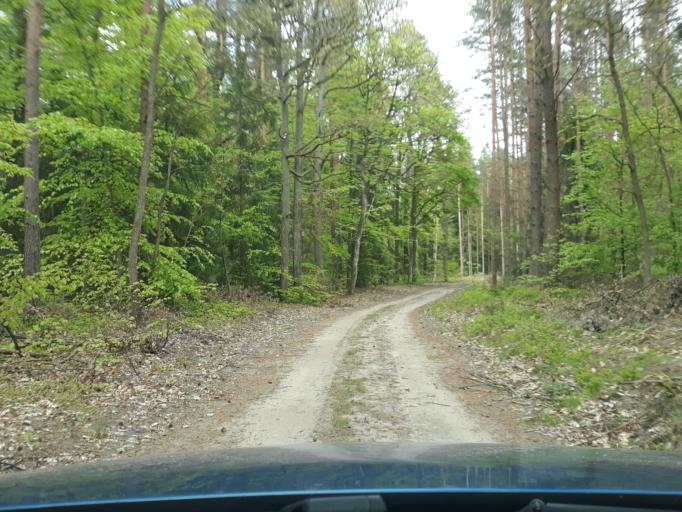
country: PL
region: Pomeranian Voivodeship
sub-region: Powiat czluchowski
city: Czluchow
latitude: 53.7567
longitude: 17.3467
